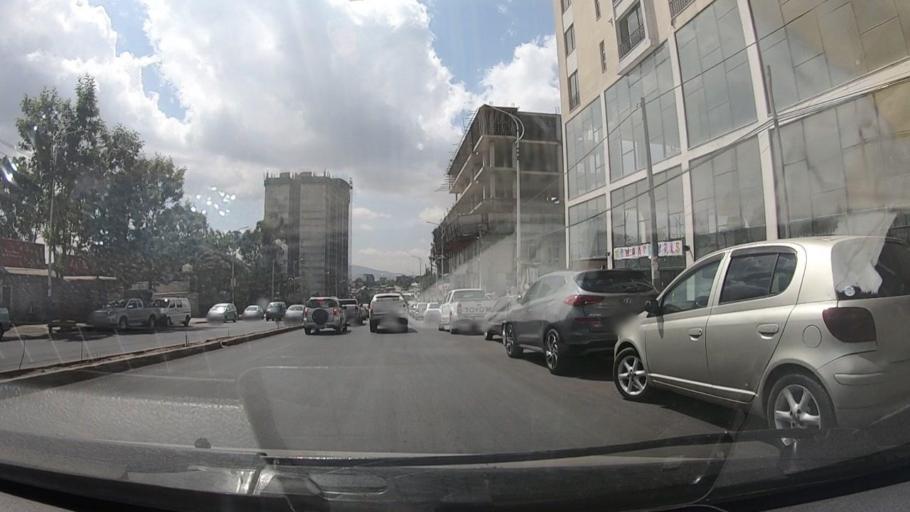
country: ET
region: Adis Abeba
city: Addis Ababa
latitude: 8.9869
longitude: 38.7215
